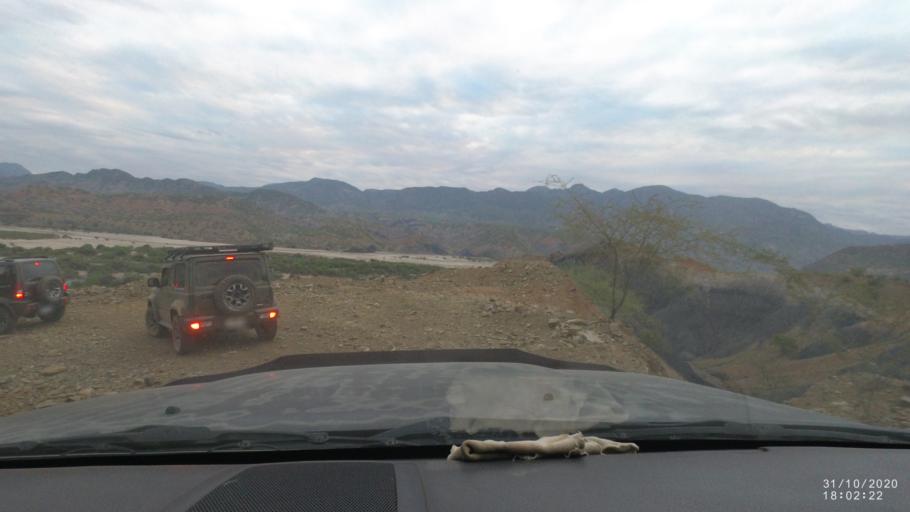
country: BO
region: Chuquisaca
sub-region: Provincia Zudanez
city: Mojocoya
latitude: -18.6661
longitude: -64.5290
